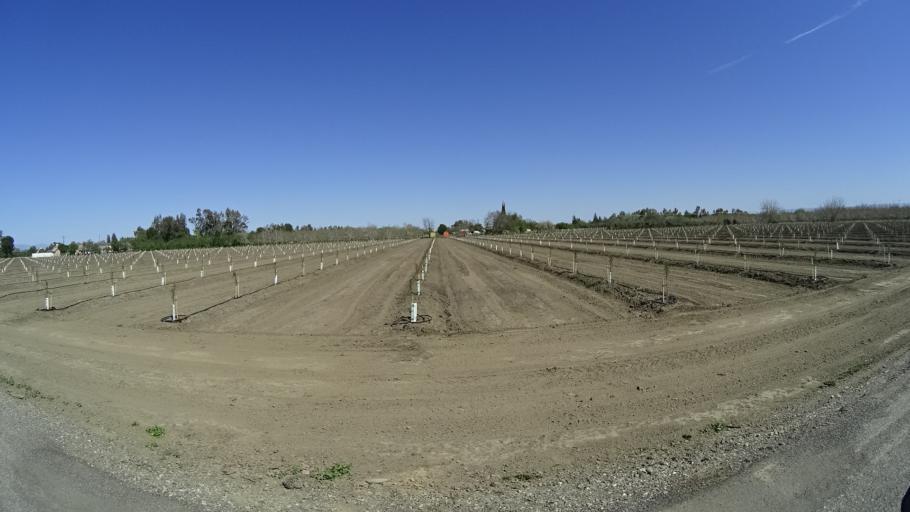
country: US
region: California
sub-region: Glenn County
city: Orland
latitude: 39.7429
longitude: -122.1248
